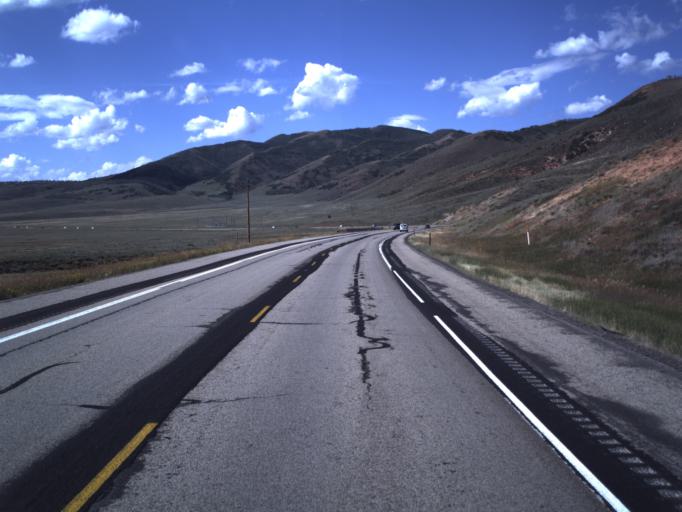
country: US
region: Utah
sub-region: Wasatch County
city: Heber
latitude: 40.2154
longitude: -111.1033
